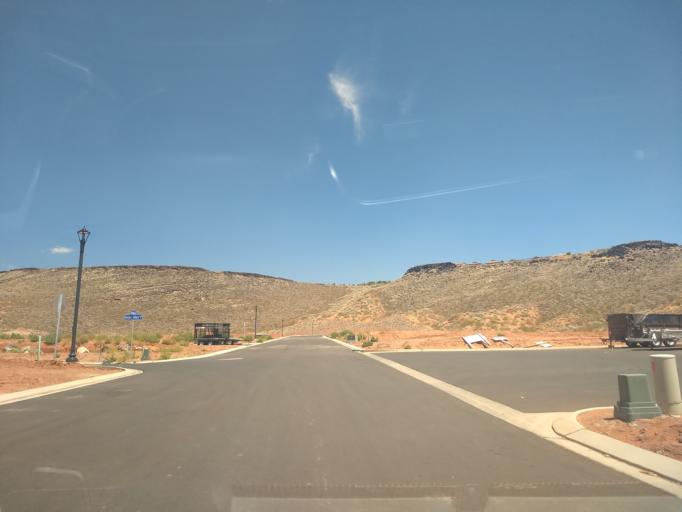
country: US
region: Utah
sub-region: Washington County
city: Washington
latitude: 37.1466
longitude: -113.4714
